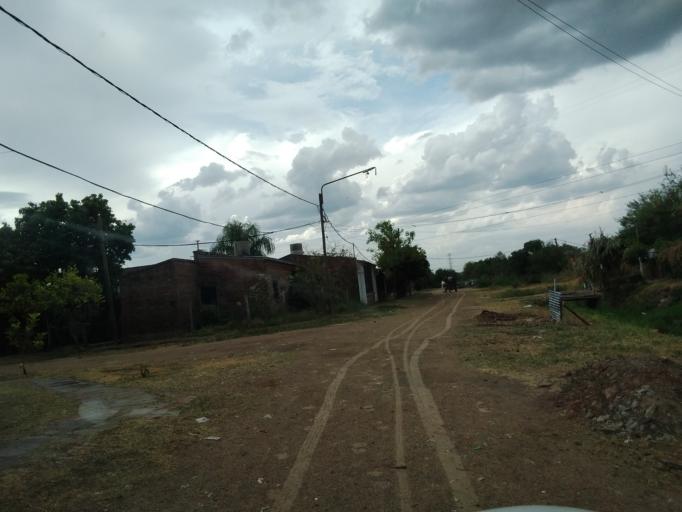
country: AR
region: Corrientes
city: Corrientes
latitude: -27.5199
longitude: -58.7879
